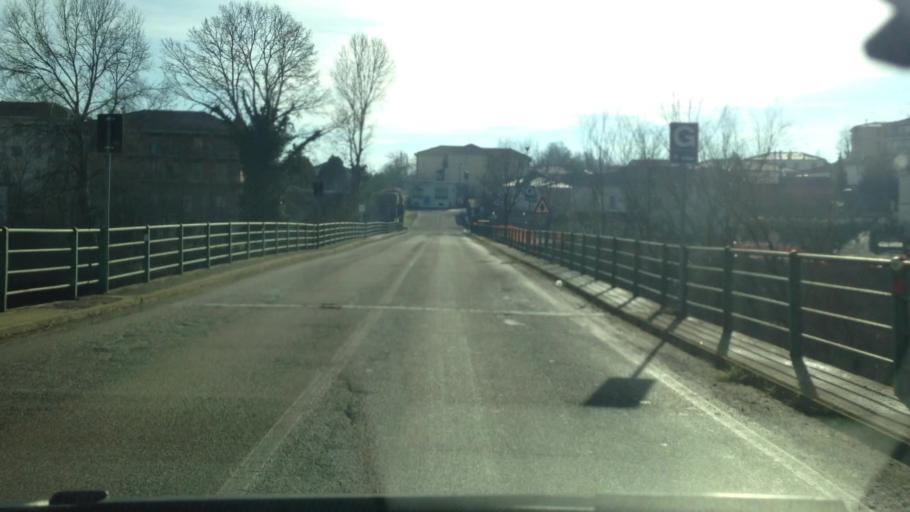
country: IT
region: Piedmont
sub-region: Provincia di Alessandria
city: Masio
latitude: 44.8723
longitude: 8.4105
